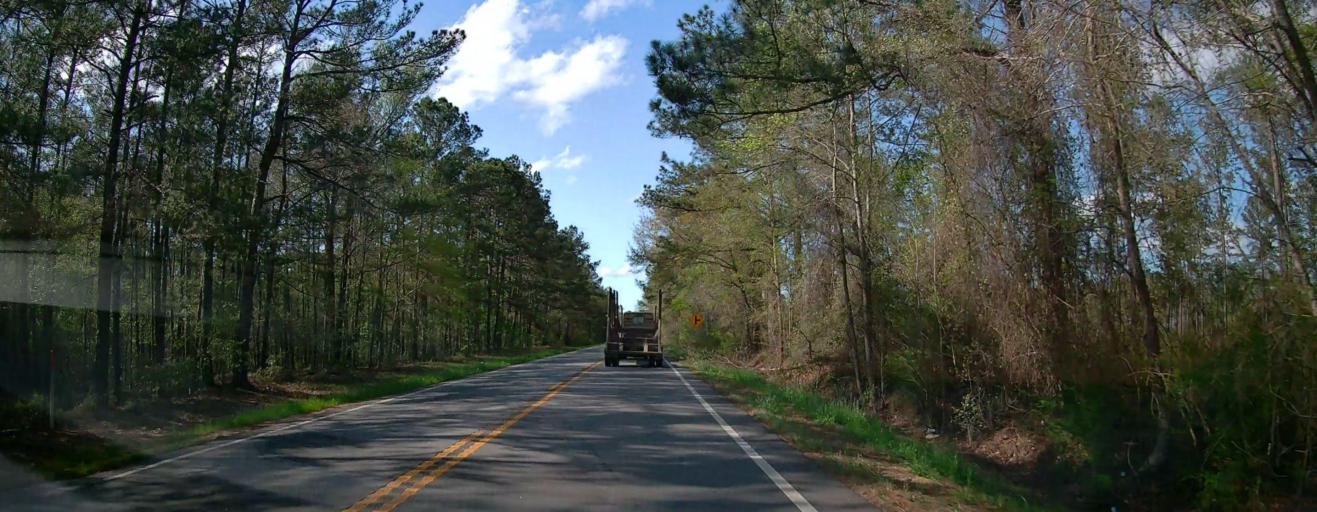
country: US
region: Georgia
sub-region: Baldwin County
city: Hardwick
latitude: 33.0513
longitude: -83.1229
